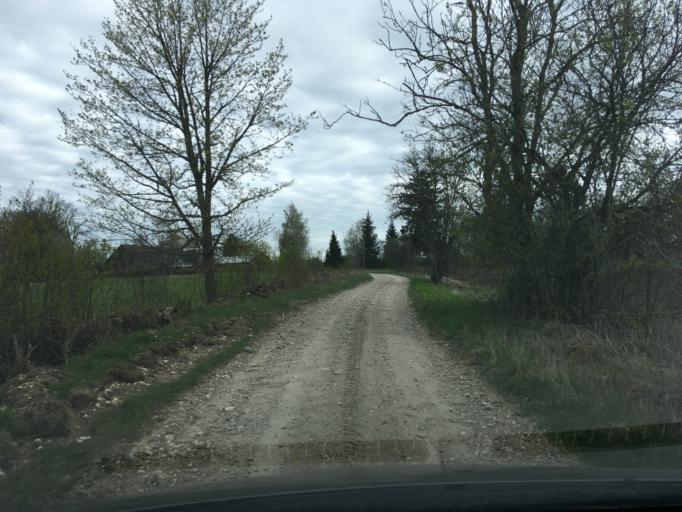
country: EE
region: Laeaene
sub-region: Lihula vald
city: Lihula
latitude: 58.5756
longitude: 23.7237
